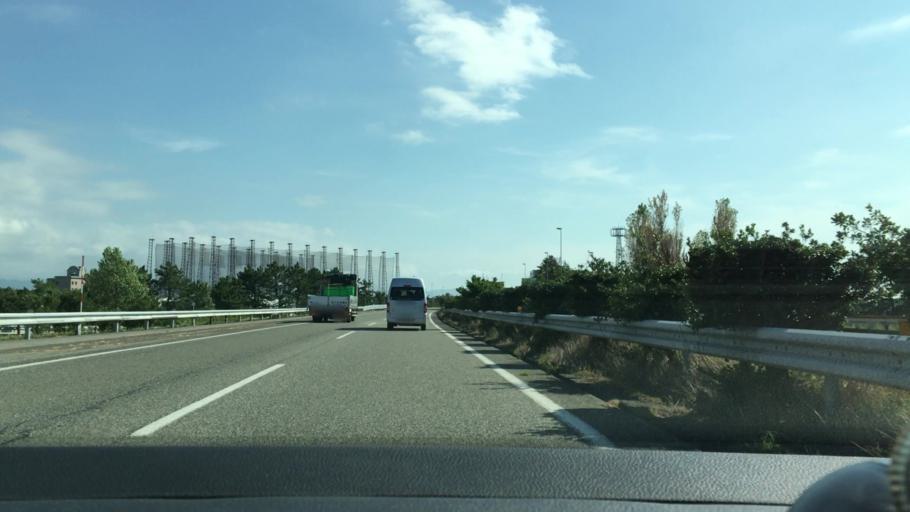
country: JP
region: Ishikawa
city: Komatsu
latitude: 36.4239
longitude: 136.4310
